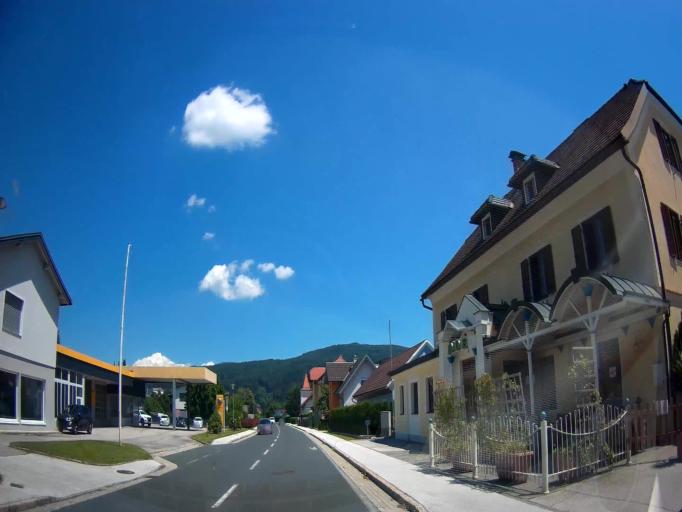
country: AT
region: Carinthia
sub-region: Politischer Bezirk Volkermarkt
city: Bleiburg/Pliberk
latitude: 46.5785
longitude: 14.7918
